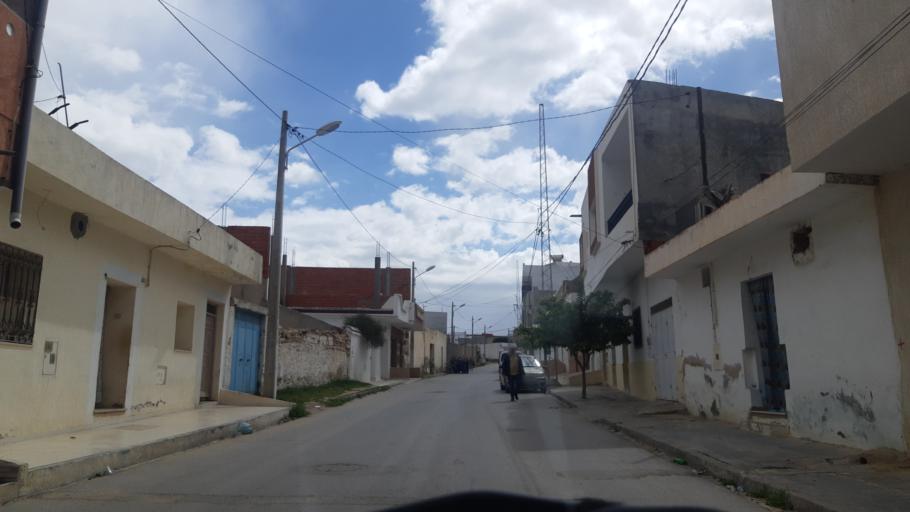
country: TN
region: Susah
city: Akouda
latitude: 35.8660
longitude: 10.5410
